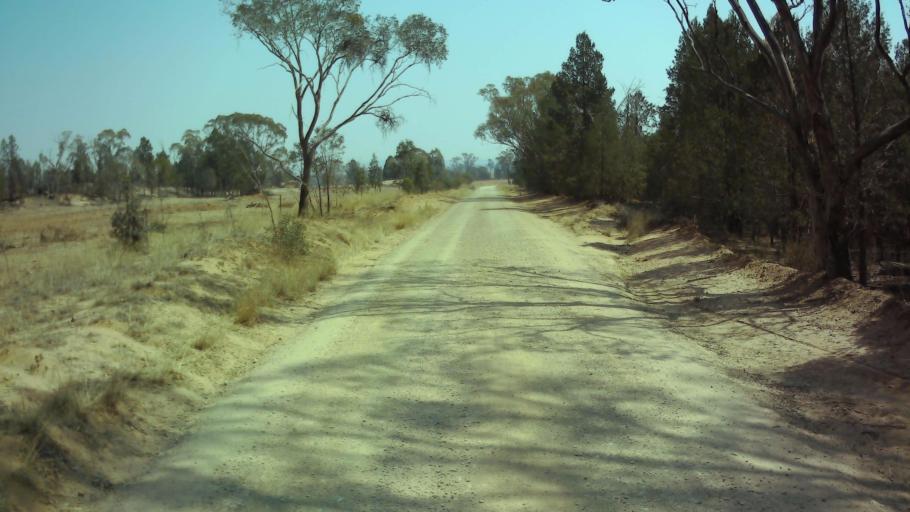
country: AU
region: New South Wales
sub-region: Weddin
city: Grenfell
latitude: -33.6521
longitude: 148.2712
